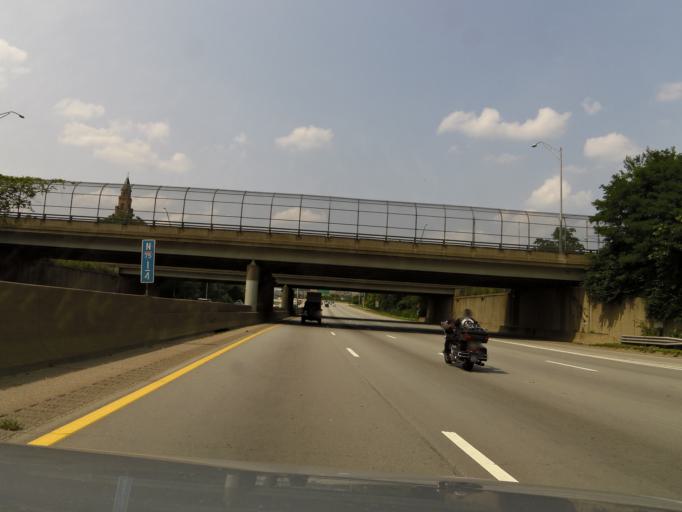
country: US
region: Kentucky
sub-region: Kenton County
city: Ludlow
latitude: 39.1089
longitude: -84.5317
